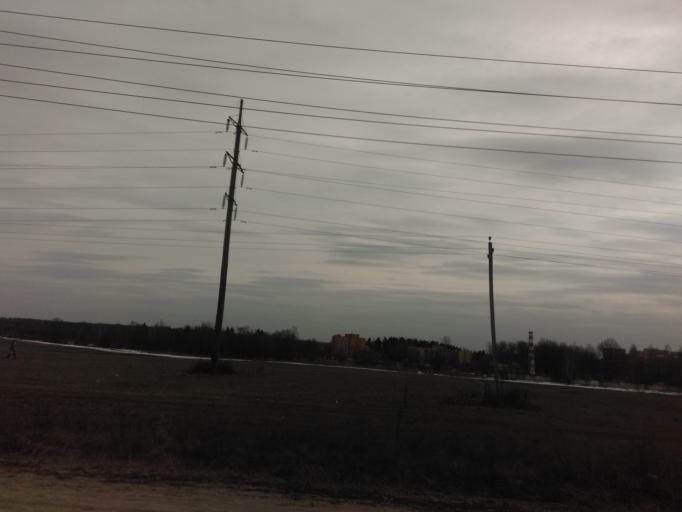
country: RU
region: Moskovskaya
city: Karinskoye
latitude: 55.7076
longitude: 36.6681
